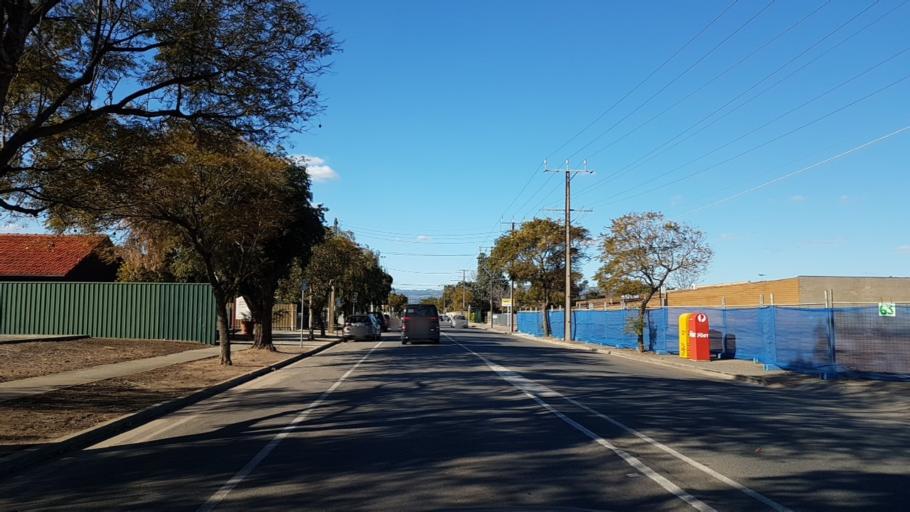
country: AU
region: South Australia
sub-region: City of West Torrens
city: Plympton
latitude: -34.9601
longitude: 138.5458
